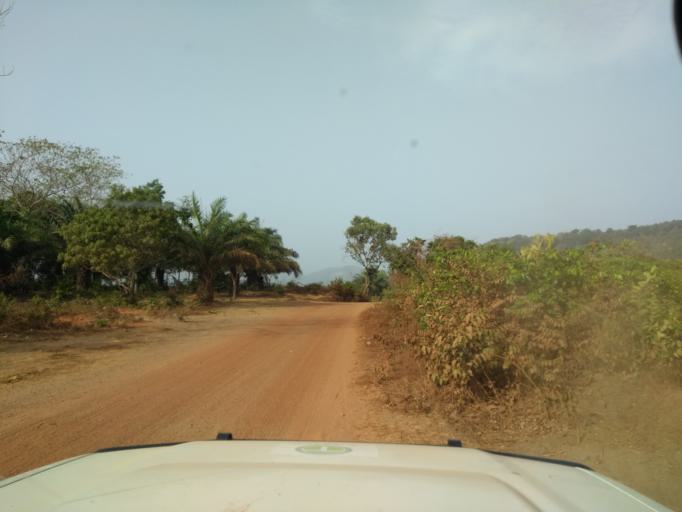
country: GN
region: Kindia
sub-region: Prefecture de Dubreka
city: Dubreka
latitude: 9.8538
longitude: -13.5522
